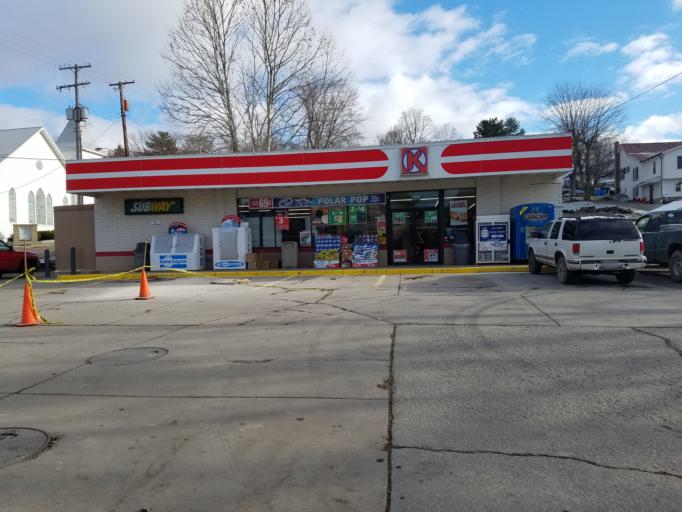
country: US
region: Ohio
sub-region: Harrison County
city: Cadiz
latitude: 40.3968
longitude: -81.0853
